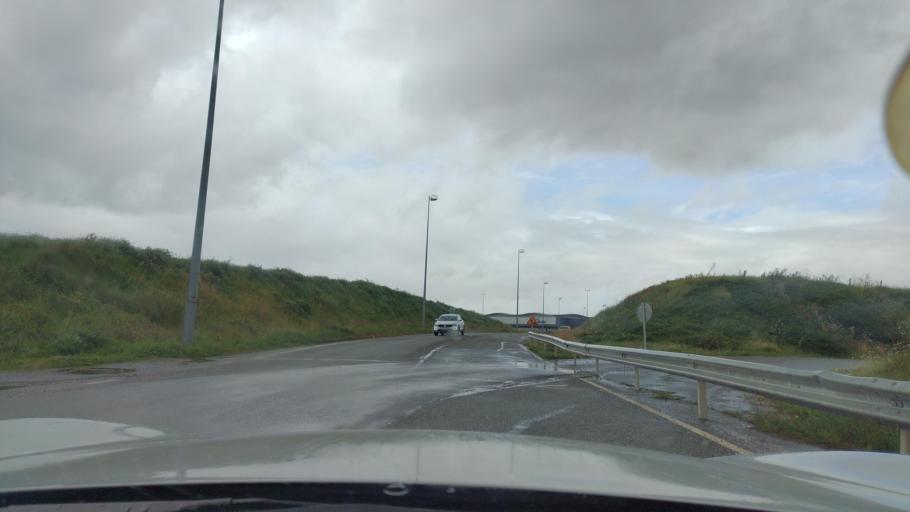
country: FR
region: Ile-de-France
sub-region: Departement de Seine-et-Marne
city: Mitry-Mory
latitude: 49.0088
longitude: 2.6015
